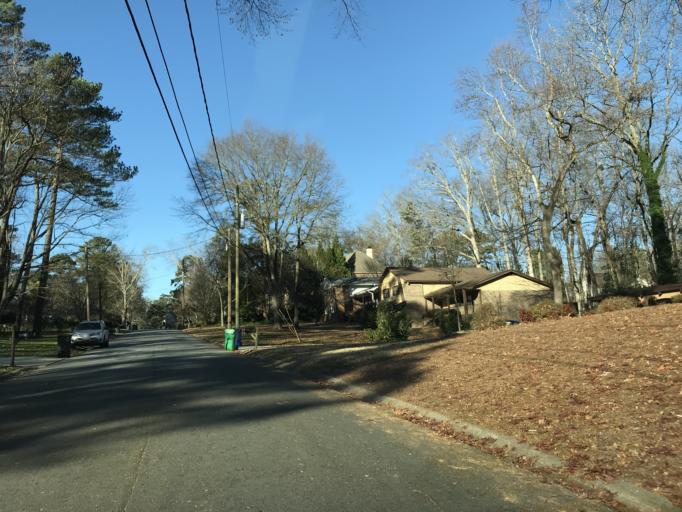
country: US
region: Georgia
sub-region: DeKalb County
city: North Atlanta
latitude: 33.8883
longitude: -84.3393
